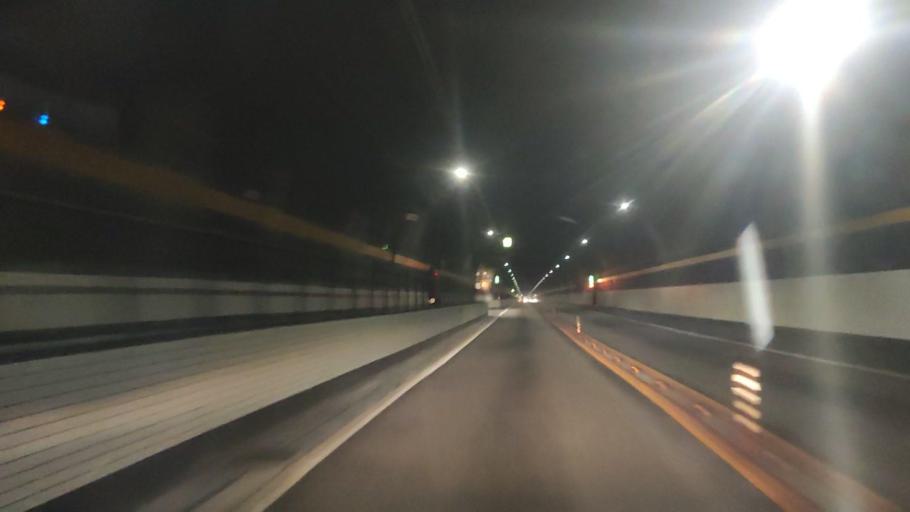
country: JP
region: Nagasaki
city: Obita
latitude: 32.7820
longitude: 129.8852
